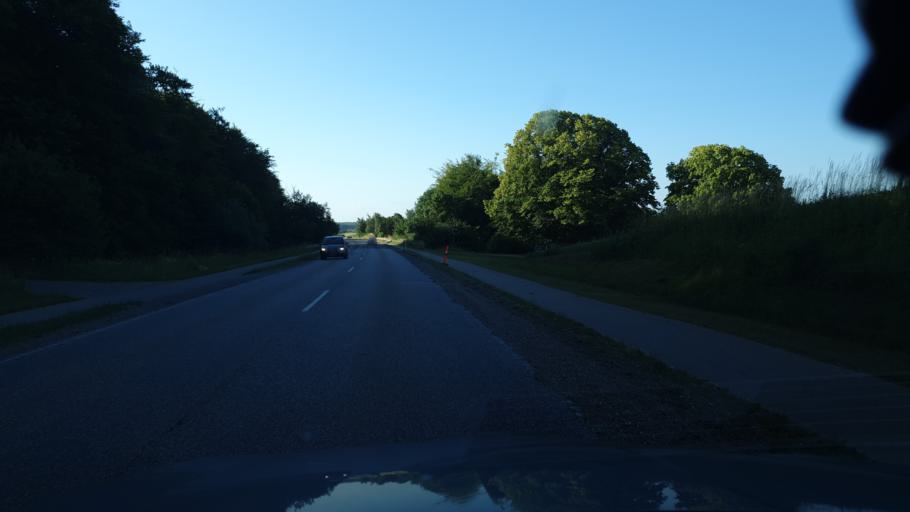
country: DK
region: Zealand
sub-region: Soro Kommune
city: Frederiksberg
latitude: 55.3956
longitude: 11.6370
